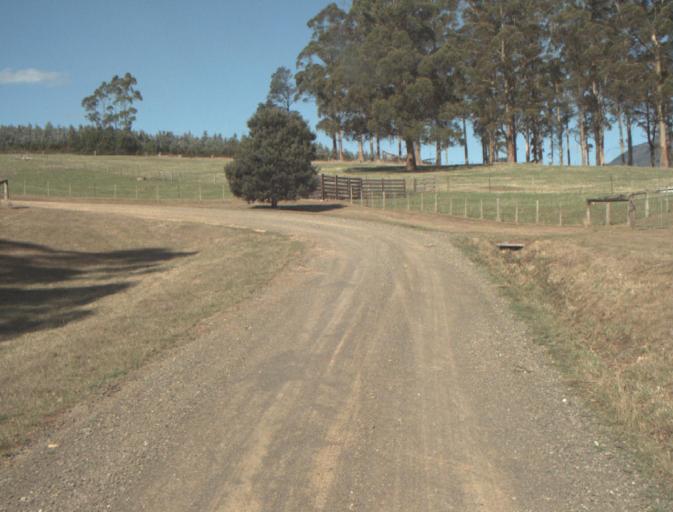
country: AU
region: Tasmania
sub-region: Launceston
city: Mayfield
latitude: -41.2223
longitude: 147.2412
